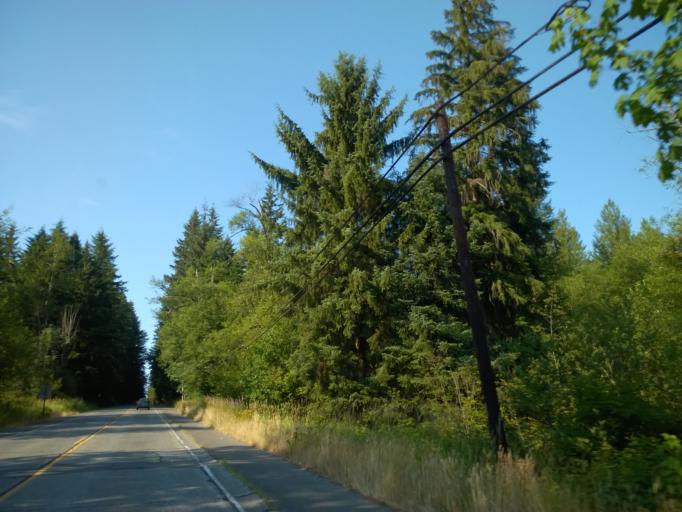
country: US
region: Washington
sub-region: King County
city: Cottage Lake
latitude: 47.7263
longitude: -122.0845
